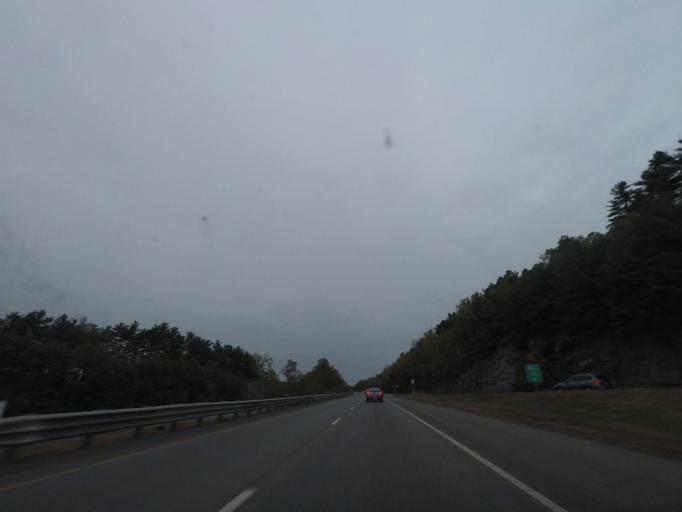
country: US
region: Massachusetts
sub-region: Worcester County
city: Oxford
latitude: 42.1193
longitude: -71.8552
